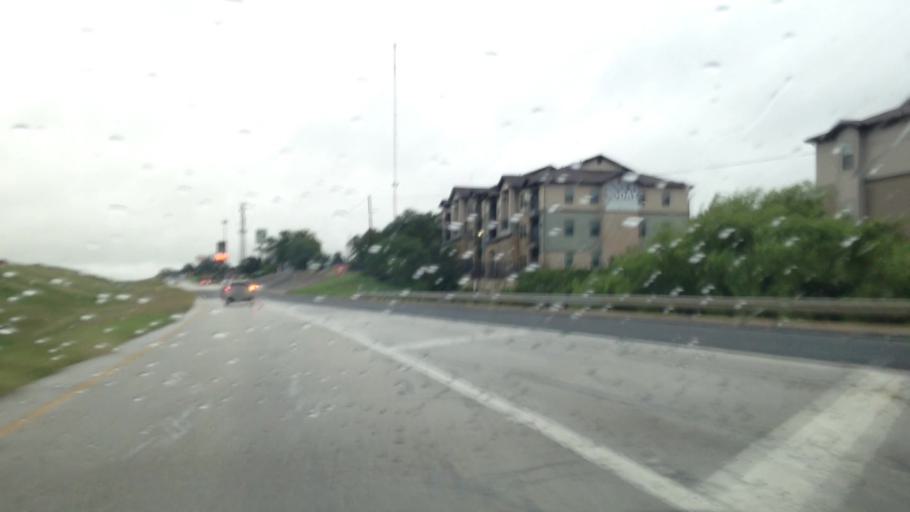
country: US
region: Texas
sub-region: Bexar County
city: Live Oak
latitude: 29.6018
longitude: -98.3912
